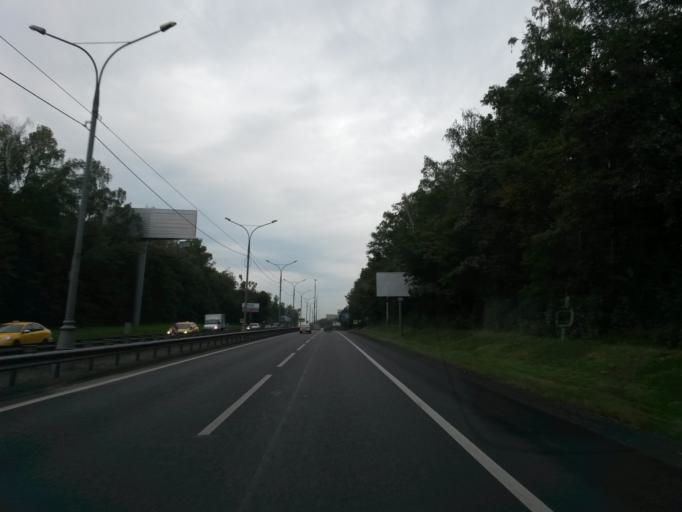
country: RU
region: Moskovskaya
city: Petrovskaya
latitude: 55.5442
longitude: 37.7990
